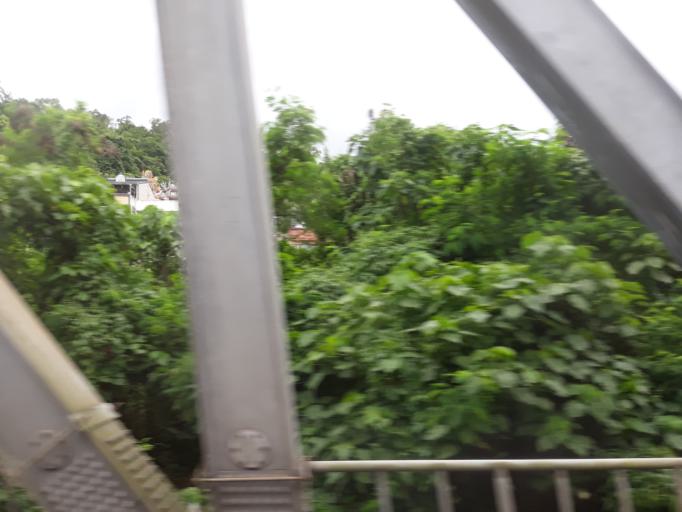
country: TW
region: Taiwan
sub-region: Yilan
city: Yilan
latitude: 24.6160
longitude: 121.8117
